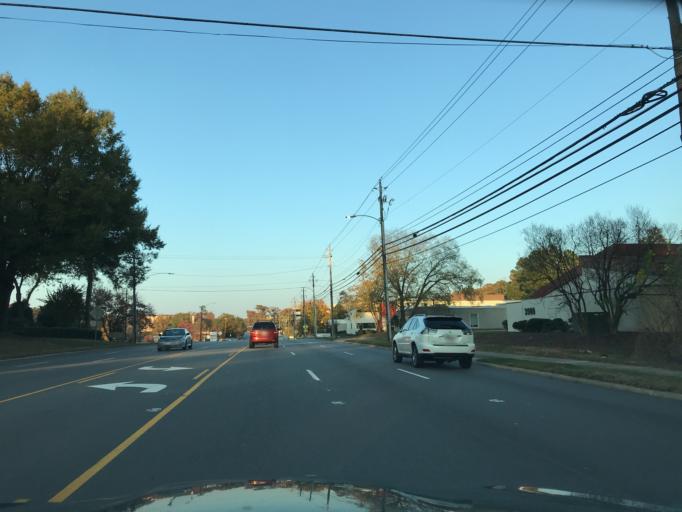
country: US
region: North Carolina
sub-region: Wake County
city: Raleigh
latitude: 35.8342
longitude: -78.6159
